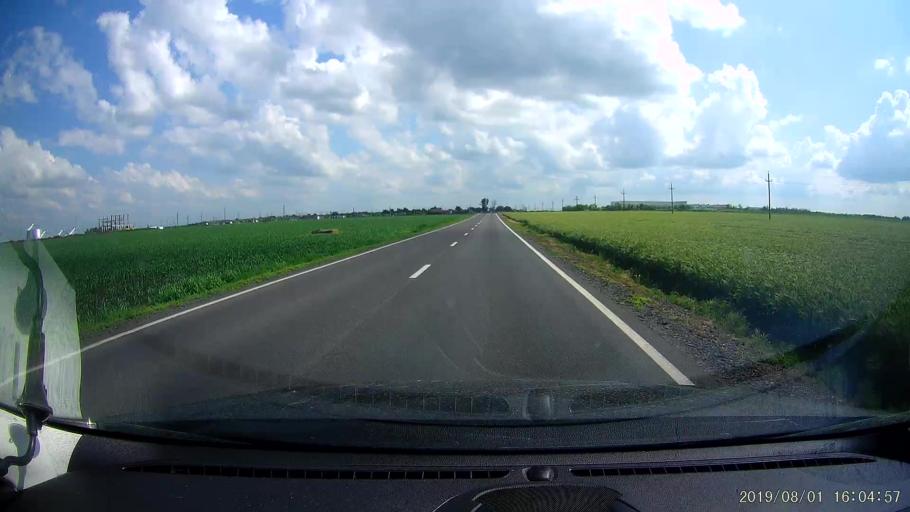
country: RO
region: Calarasi
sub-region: Comuna Dragalina
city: Drajna Noua
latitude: 44.4349
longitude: 27.3779
